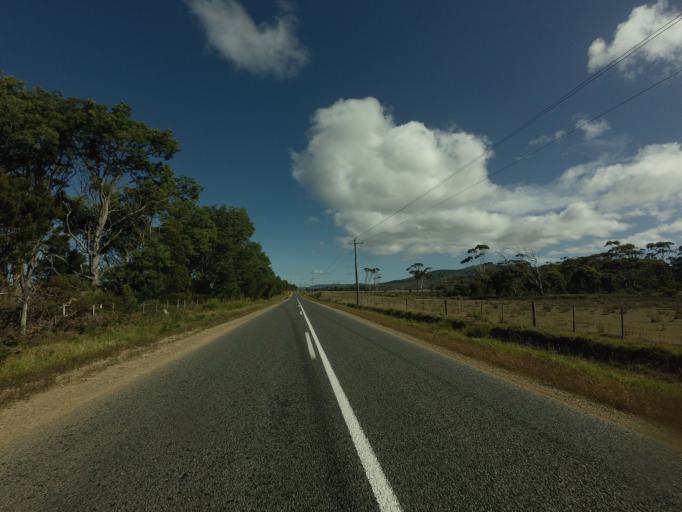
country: AU
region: Tasmania
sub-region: Break O'Day
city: St Helens
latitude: -41.7641
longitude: 148.2721
